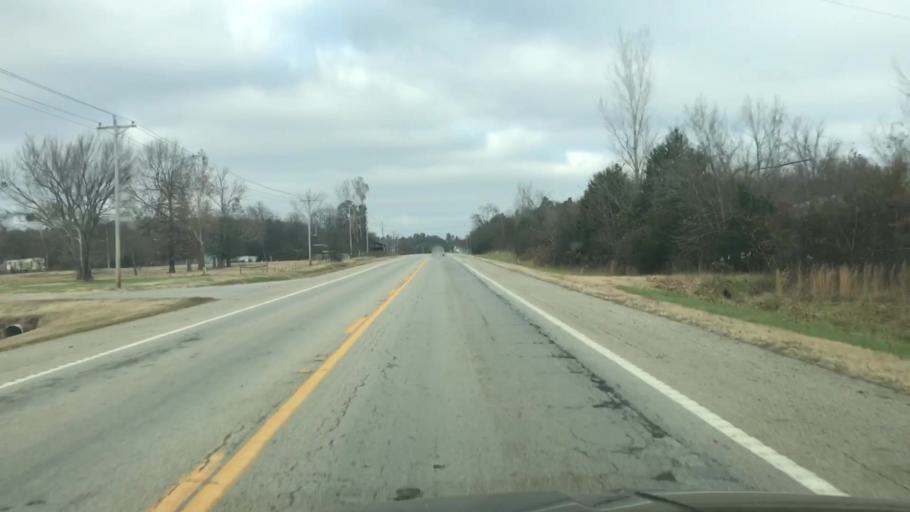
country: US
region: Arkansas
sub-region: Scott County
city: Waldron
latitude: 34.8497
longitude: -94.0611
